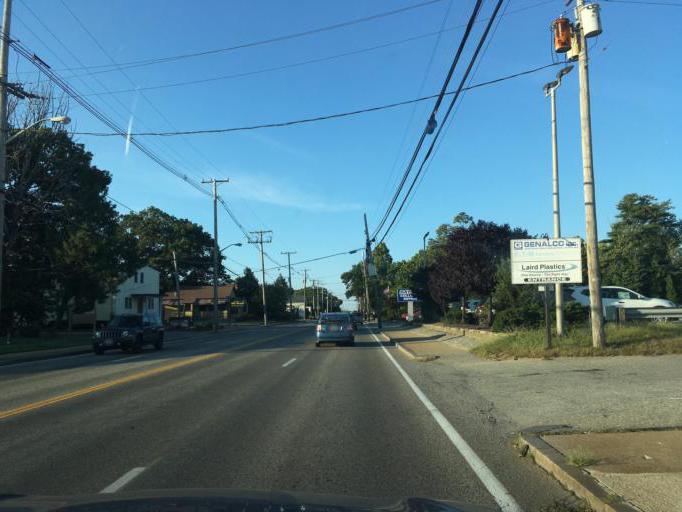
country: US
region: Rhode Island
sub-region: Providence County
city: Cranston
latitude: 41.7376
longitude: -71.4398
